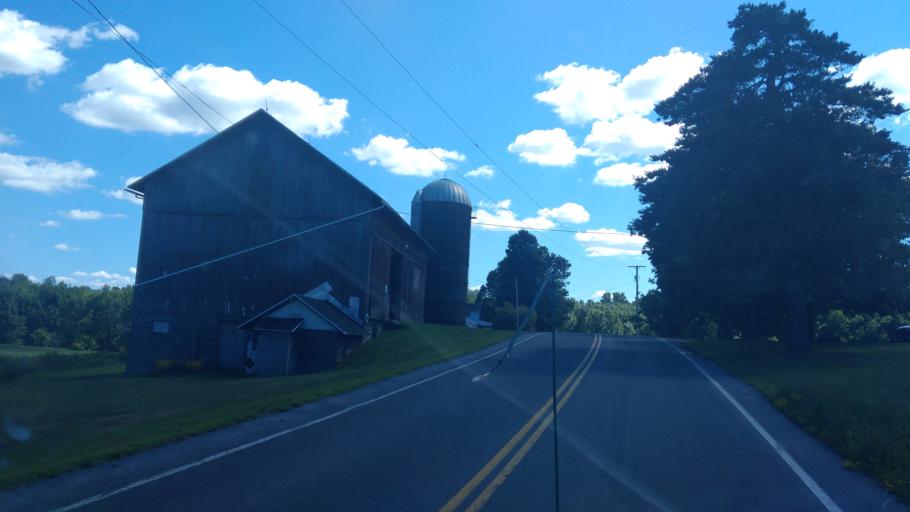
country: US
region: New York
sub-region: Wayne County
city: Lyons
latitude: 43.1547
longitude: -77.0145
